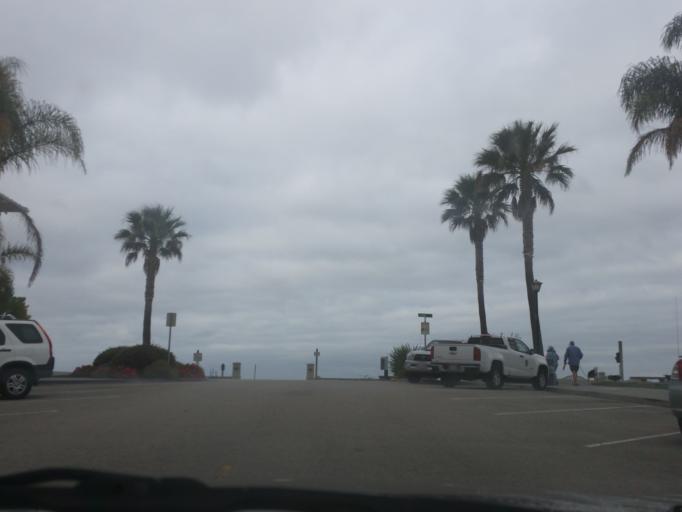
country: US
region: California
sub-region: San Luis Obispo County
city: Avila Beach
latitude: 35.1798
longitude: -120.7359
